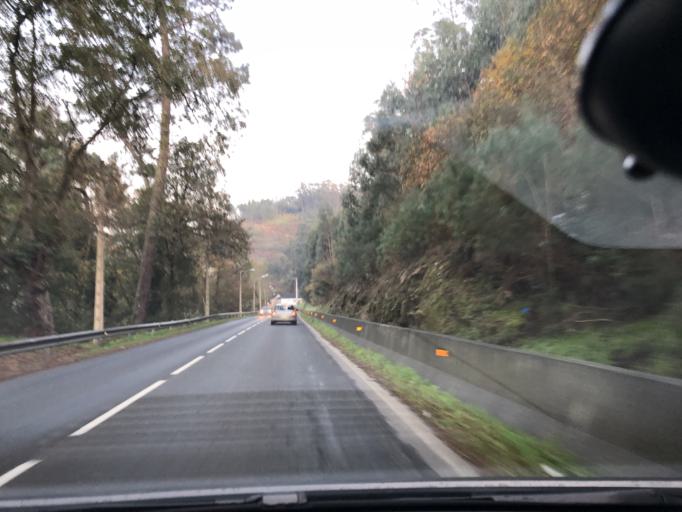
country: ES
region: Galicia
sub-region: Provincia de Pontevedra
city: Marin
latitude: 42.3820
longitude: -8.7202
